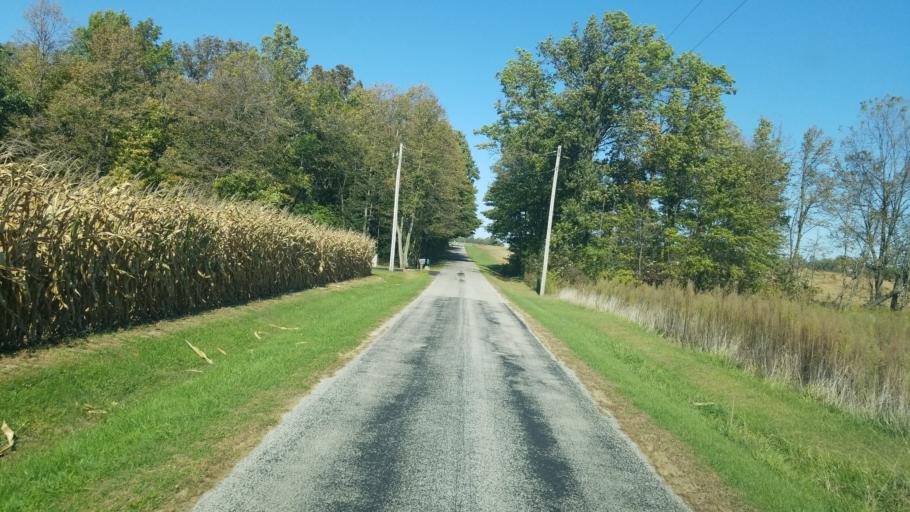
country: US
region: Ohio
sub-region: Huron County
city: Willard
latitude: 41.0377
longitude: -82.7651
